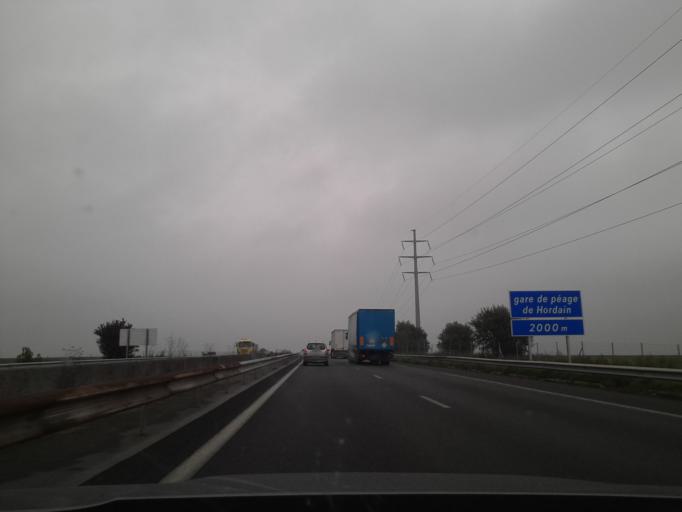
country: FR
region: Nord-Pas-de-Calais
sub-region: Departement du Nord
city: Iwuy
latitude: 50.2402
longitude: 3.2955
